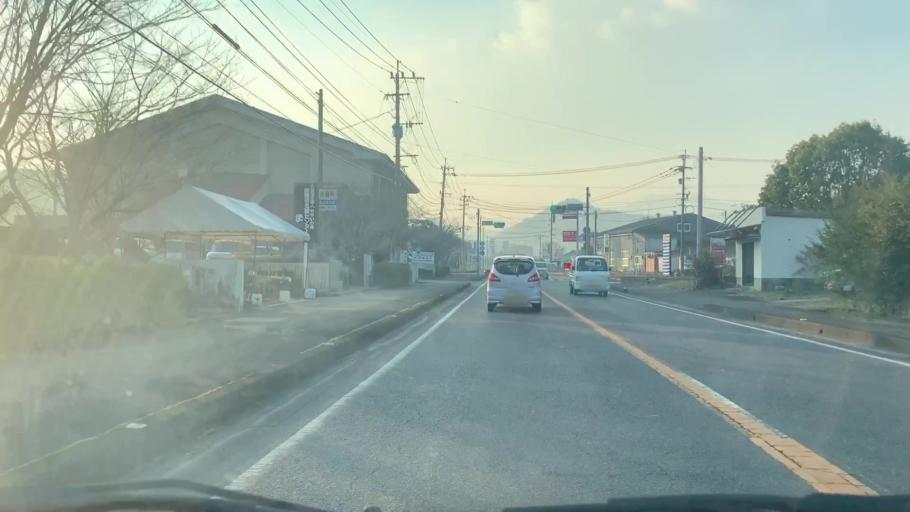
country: JP
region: Saga Prefecture
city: Takeocho-takeo
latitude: 33.2721
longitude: 130.1260
